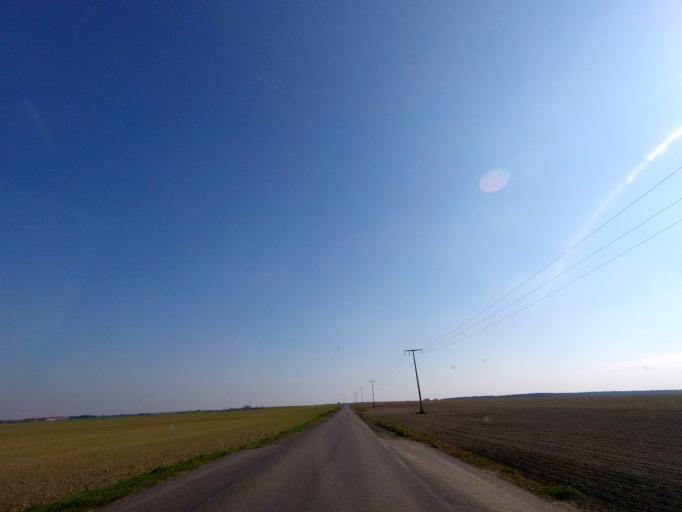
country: DE
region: Brandenburg
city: Niedergorsdorf
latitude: 51.9425
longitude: 13.0122
